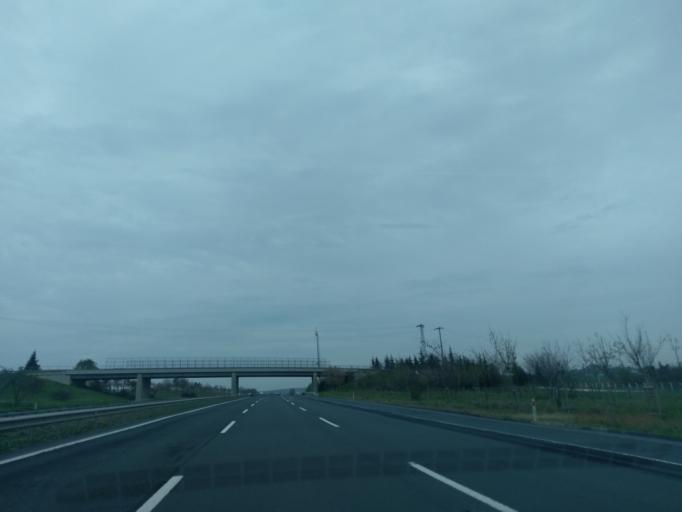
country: TR
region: Istanbul
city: Canta
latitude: 41.1396
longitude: 28.1503
